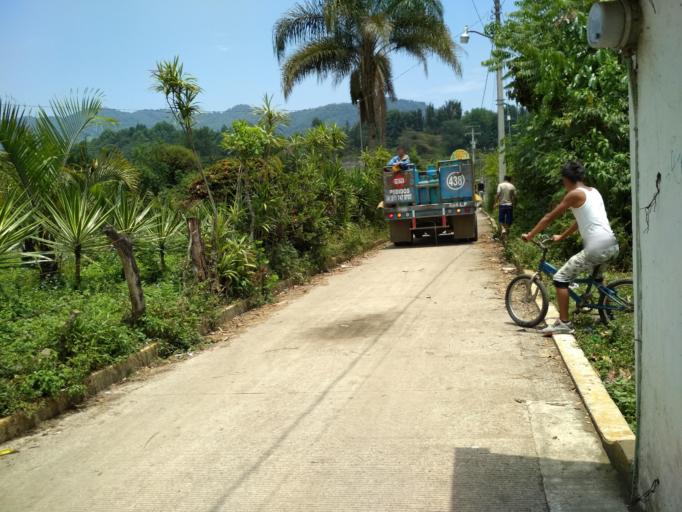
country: MX
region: Veracruz
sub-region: Mariano Escobedo
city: Mariano Escobedo
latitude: 18.9144
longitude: -97.1289
